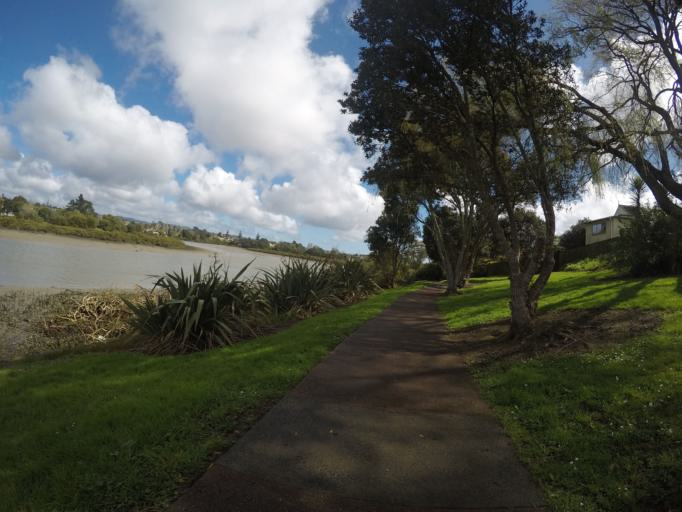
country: NZ
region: Auckland
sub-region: Auckland
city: Rosebank
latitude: -36.8978
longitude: 174.6788
